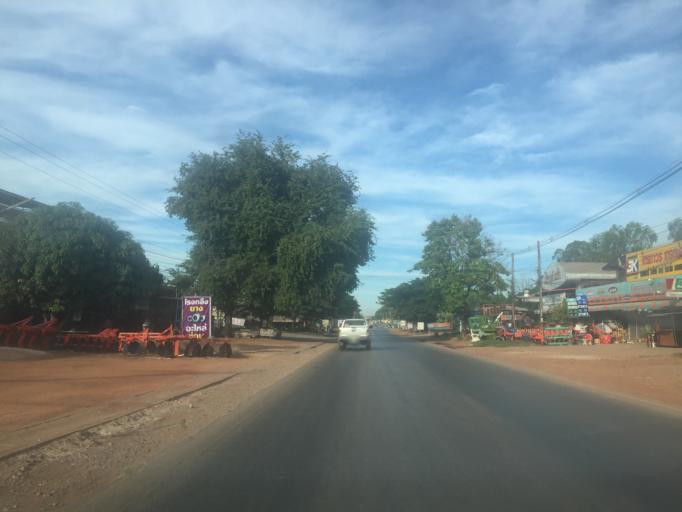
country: TH
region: Changwat Udon Thani
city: Si That
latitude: 16.9741
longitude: 103.2244
